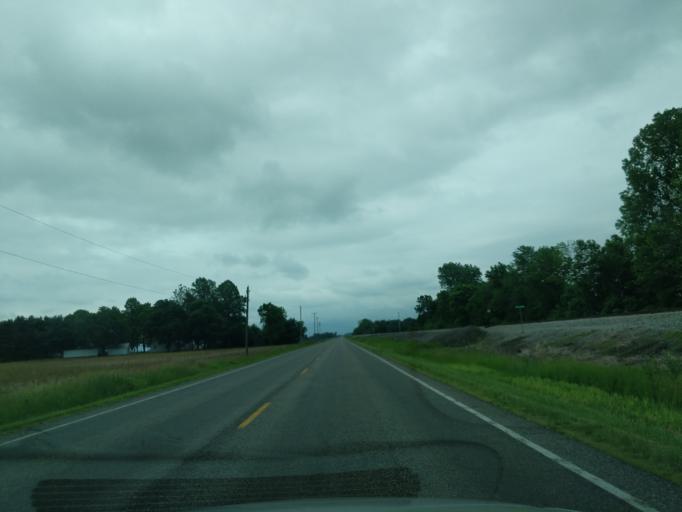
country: US
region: Indiana
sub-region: Madison County
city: Elwood
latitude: 40.2809
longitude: -85.9225
